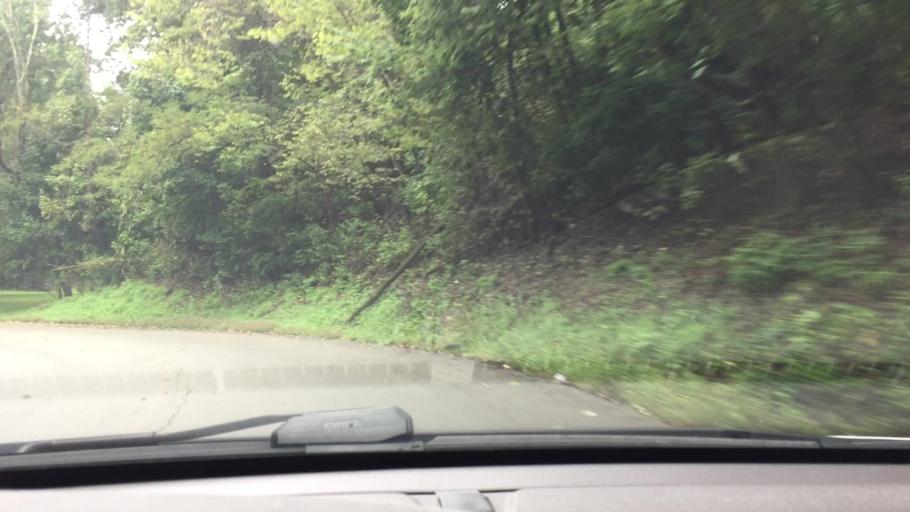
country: US
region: Pennsylvania
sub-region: Westmoreland County
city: North Belle Vernon
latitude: 40.1455
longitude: -79.8619
